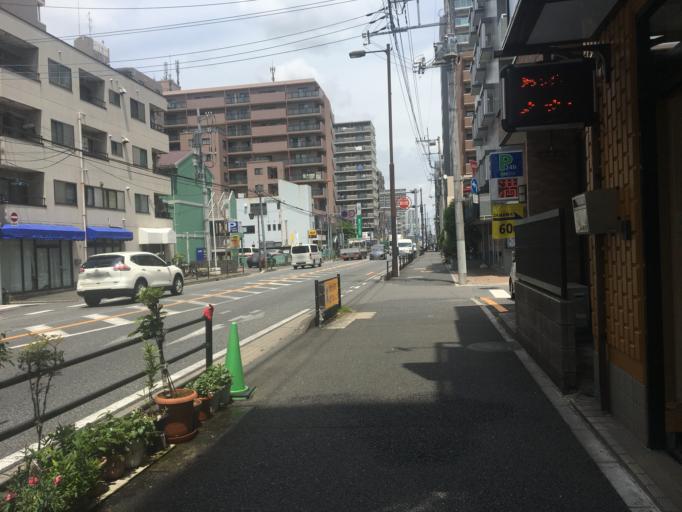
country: JP
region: Saitama
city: Shimotoda
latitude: 35.8089
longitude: 139.6830
